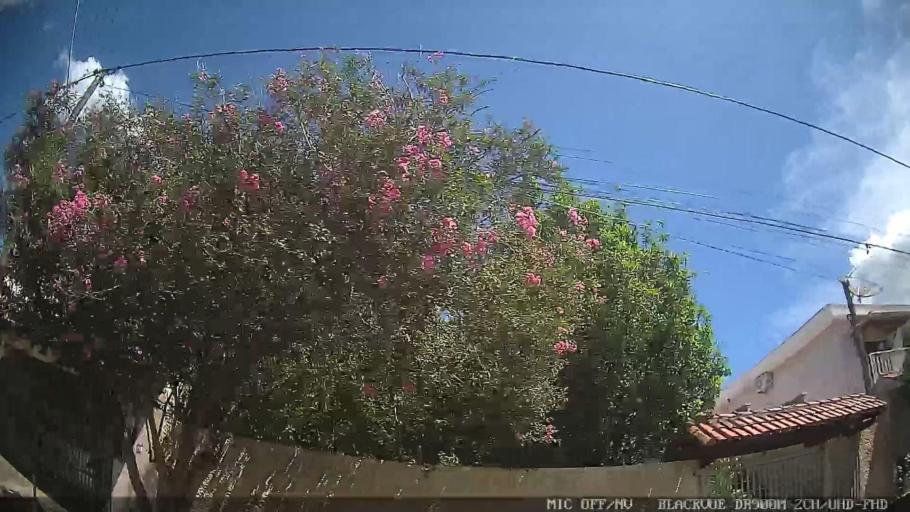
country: BR
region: Sao Paulo
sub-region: Pedreira
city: Pedreira
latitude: -22.7472
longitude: -46.9144
